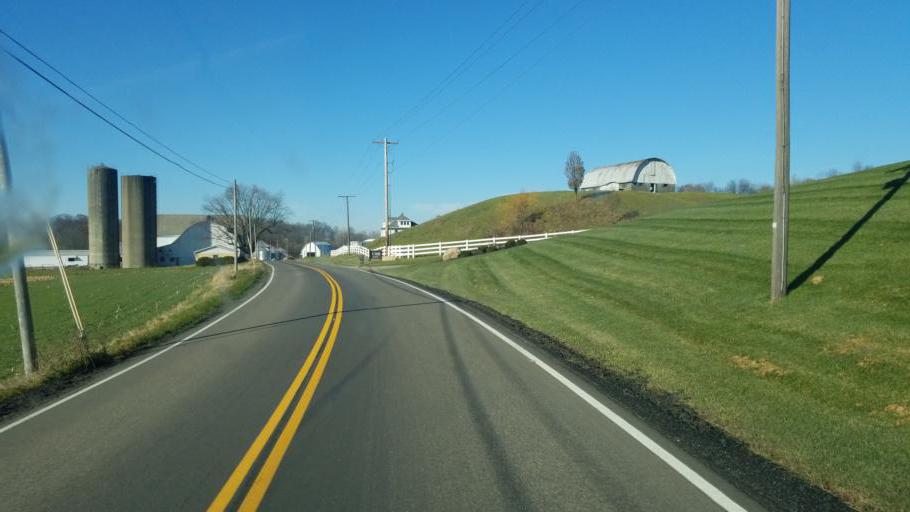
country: US
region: Ohio
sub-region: Holmes County
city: Millersburg
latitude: 40.6085
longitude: -81.8544
